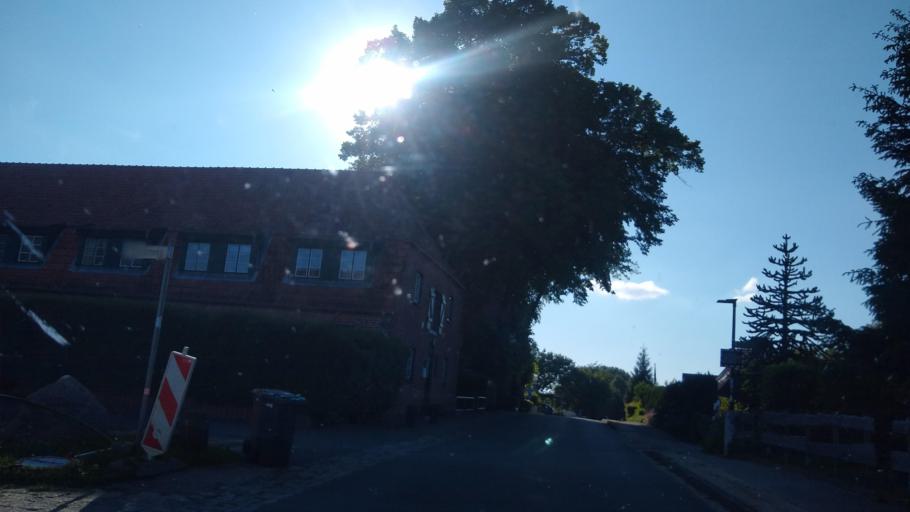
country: DE
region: Schleswig-Holstein
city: Neudorf-Bornstein
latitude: 54.4188
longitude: 9.9203
